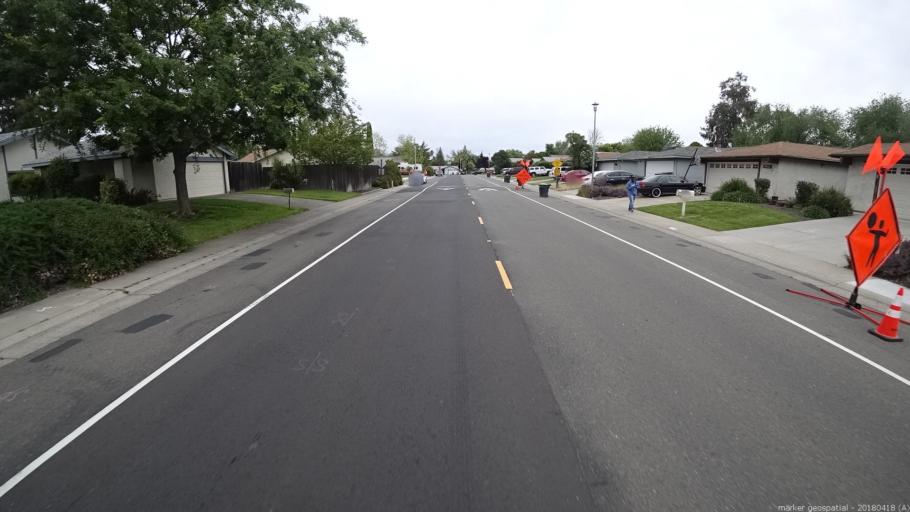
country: US
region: California
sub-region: Sacramento County
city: La Riviera
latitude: 38.5677
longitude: -121.3492
